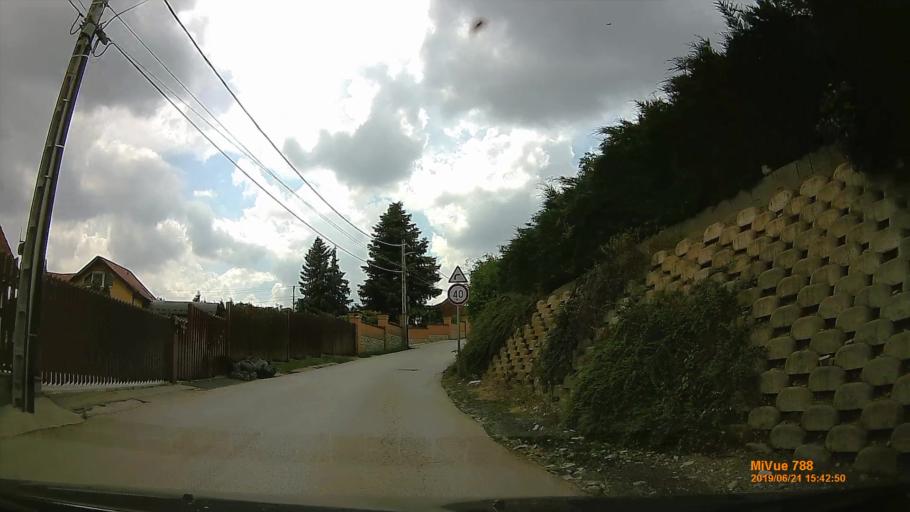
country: HU
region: Baranya
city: Pecs
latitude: 46.0831
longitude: 18.2034
